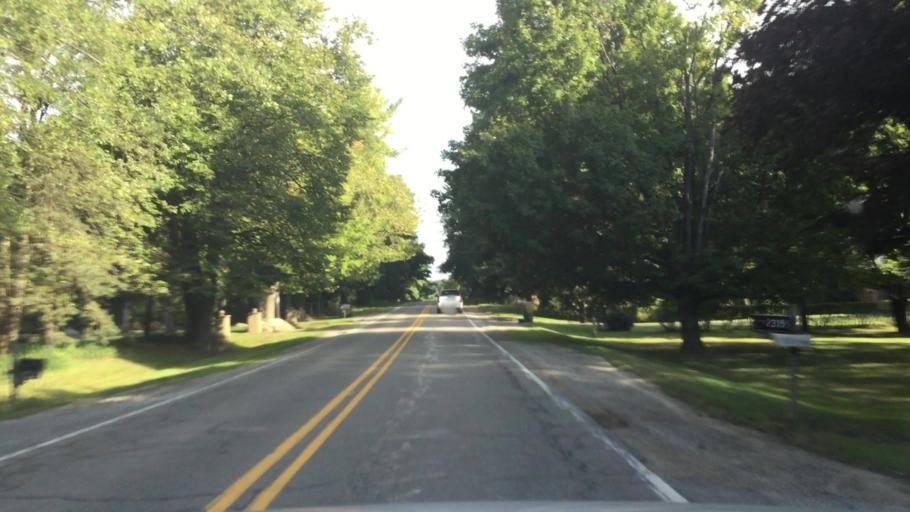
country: US
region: Michigan
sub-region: Livingston County
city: Howell
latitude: 42.5657
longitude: -83.8929
